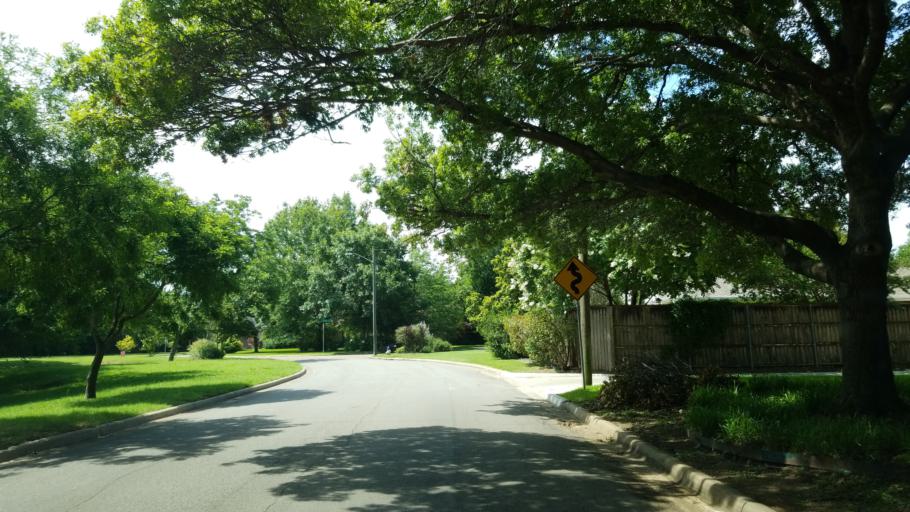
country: US
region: Texas
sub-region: Dallas County
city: Farmers Branch
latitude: 32.9087
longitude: -96.8469
